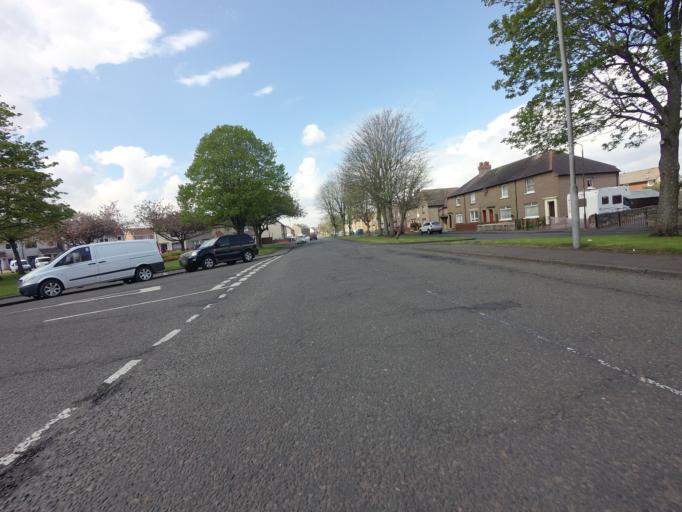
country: GB
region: Scotland
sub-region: Falkirk
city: Falkirk
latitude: 56.0267
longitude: -3.7762
